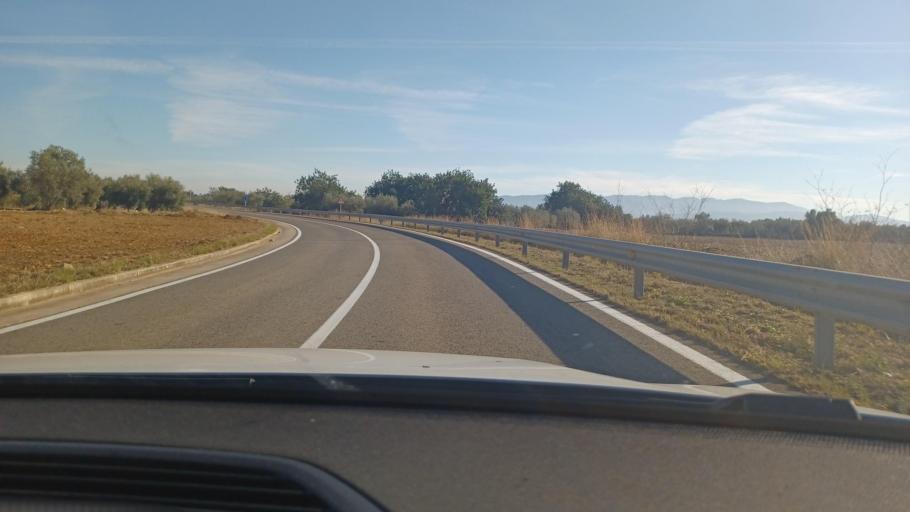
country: ES
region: Catalonia
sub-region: Provincia de Tarragona
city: Santa Barbara
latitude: 40.7197
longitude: 0.4475
